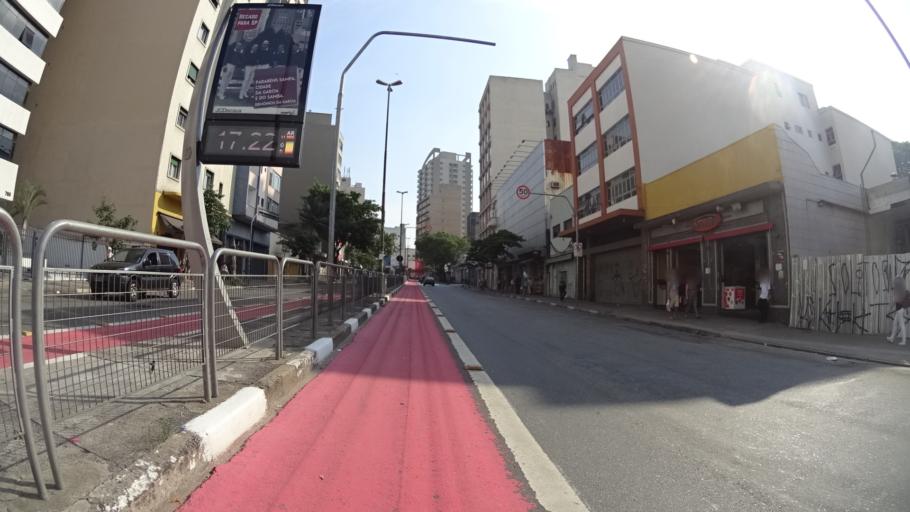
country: BR
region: Sao Paulo
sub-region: Sao Paulo
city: Sao Paulo
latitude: -23.5593
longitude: -46.6376
